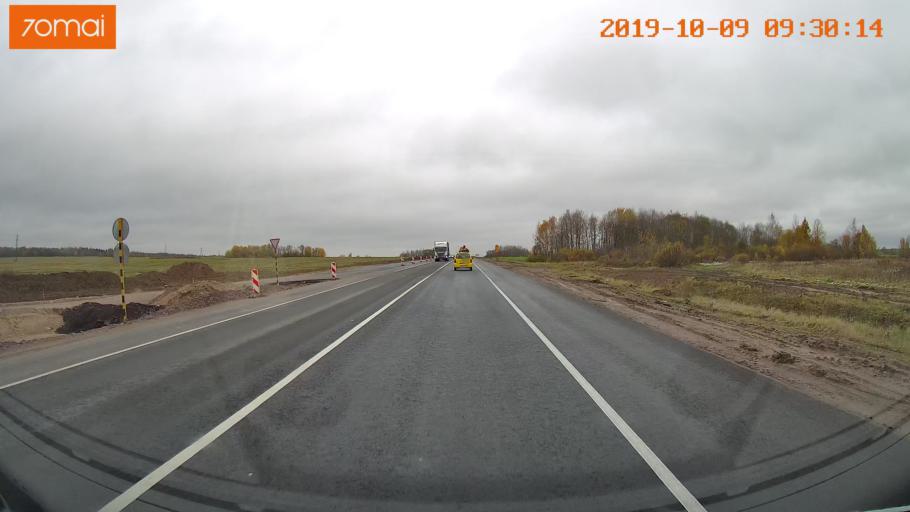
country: RU
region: Vologda
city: Vologda
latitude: 59.1381
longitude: 39.9510
